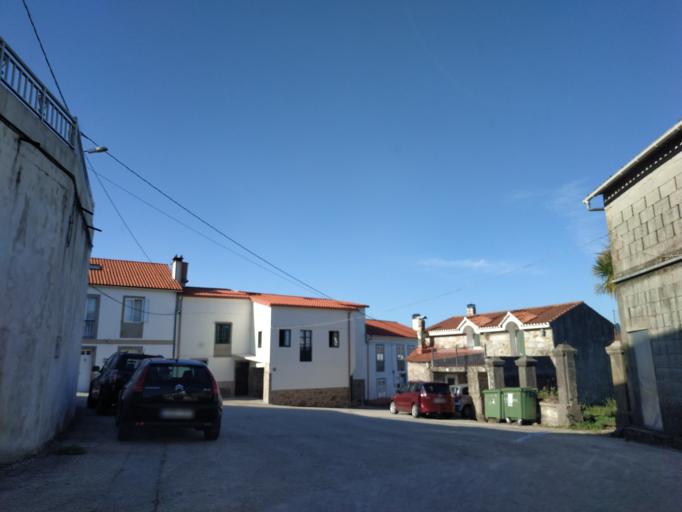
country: ES
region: Galicia
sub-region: Provincia da Coruna
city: Negreira
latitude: 42.9123
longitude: -8.7648
